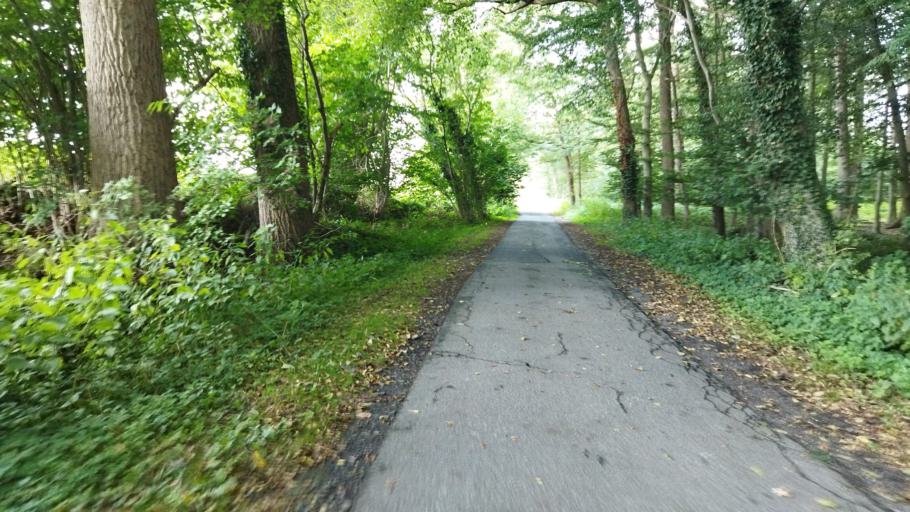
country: DE
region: North Rhine-Westphalia
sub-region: Regierungsbezirk Munster
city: Warendorf
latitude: 51.9617
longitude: 7.9283
